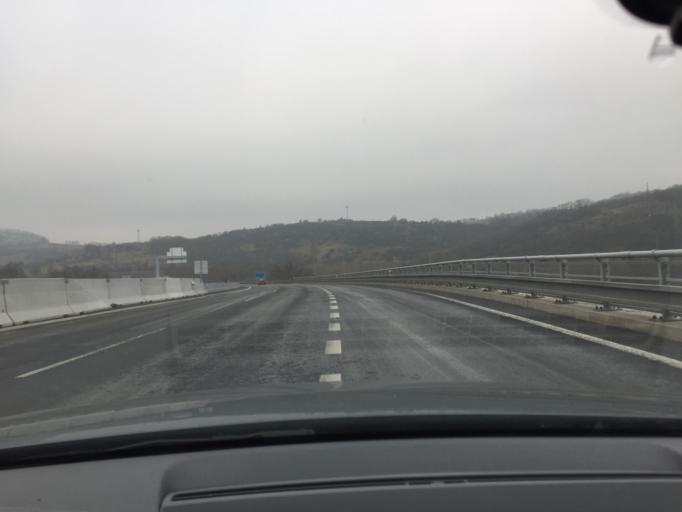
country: CZ
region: Ustecky
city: Rehlovice
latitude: 50.6136
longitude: 13.9603
